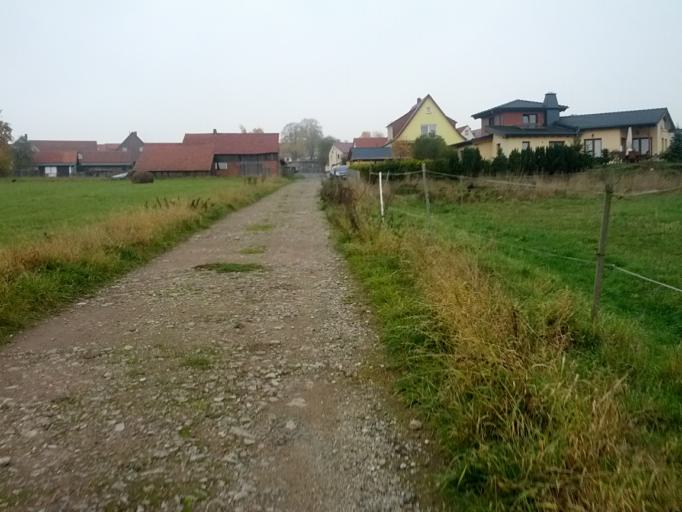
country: DE
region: Thuringia
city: Bischofroda
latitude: 50.9926
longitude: 10.4048
